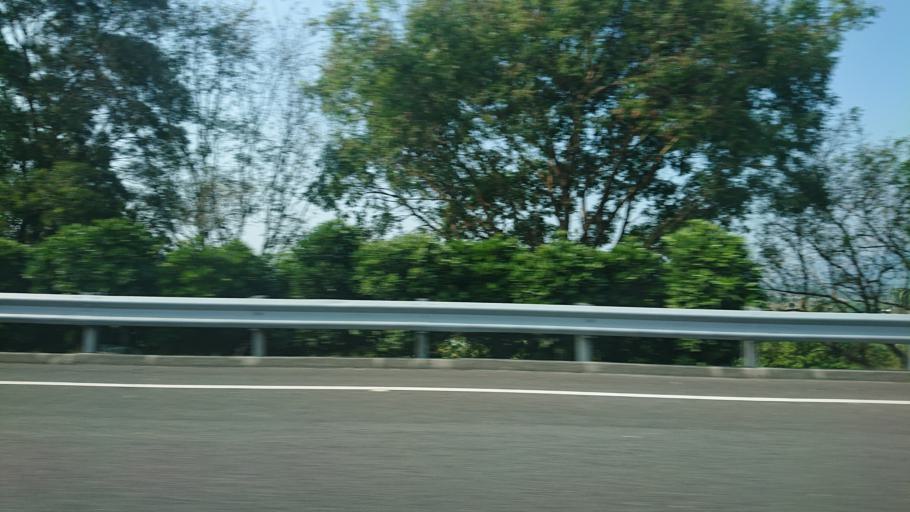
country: TW
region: Taiwan
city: Lugu
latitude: 23.7996
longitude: 120.7001
